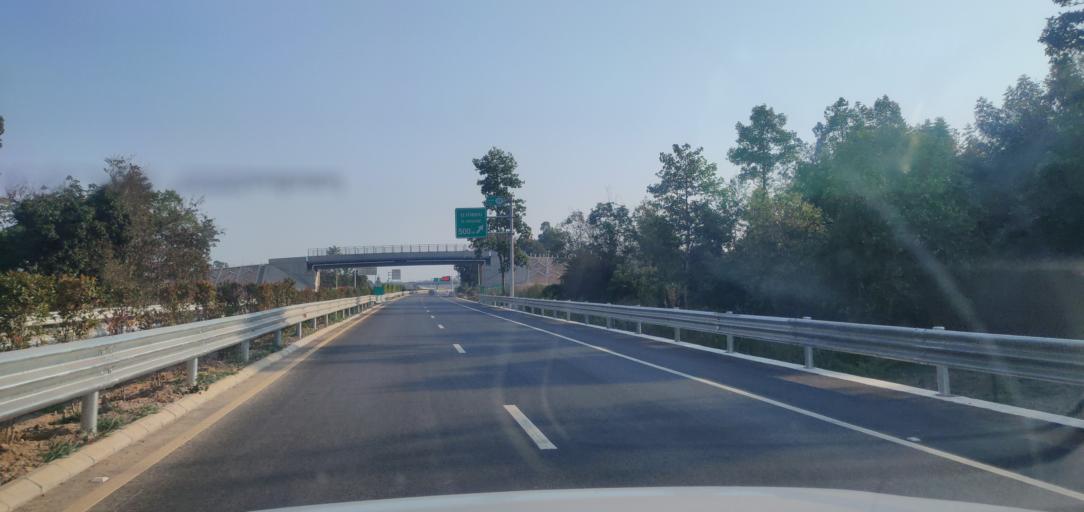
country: LA
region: Vientiane
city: Vientiane
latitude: 18.1227
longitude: 102.5021
